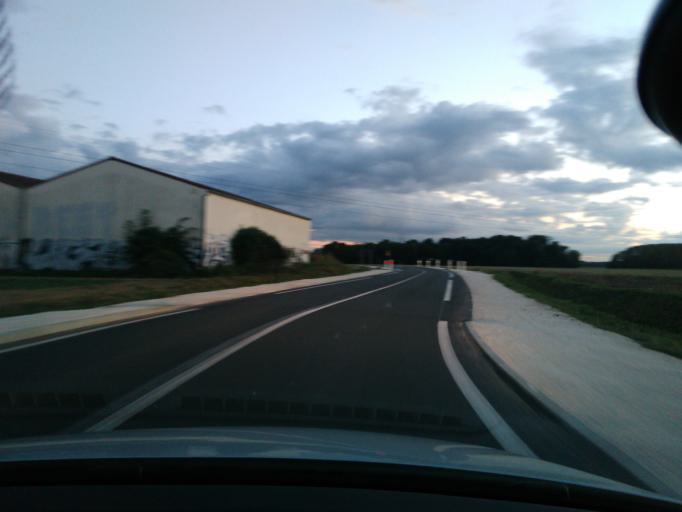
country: FR
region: Ile-de-France
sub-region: Departement de Seine-et-Marne
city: Bailly-Romainvilliers
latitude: 48.8529
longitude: 2.8471
